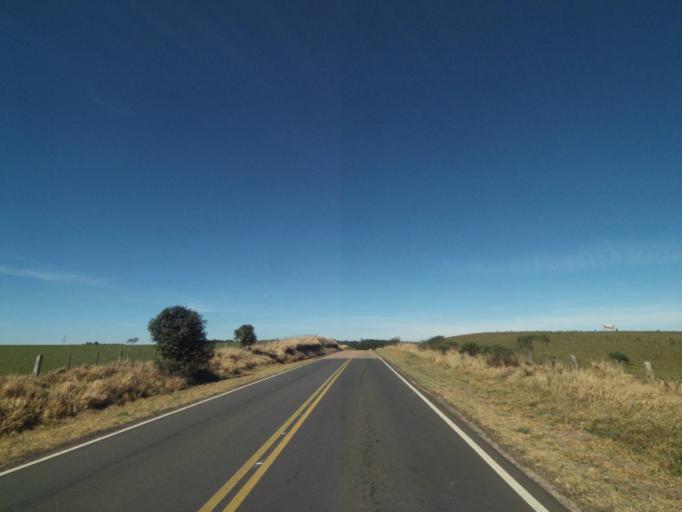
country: BR
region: Parana
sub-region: Tibagi
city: Tibagi
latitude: -24.6442
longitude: -50.2329
